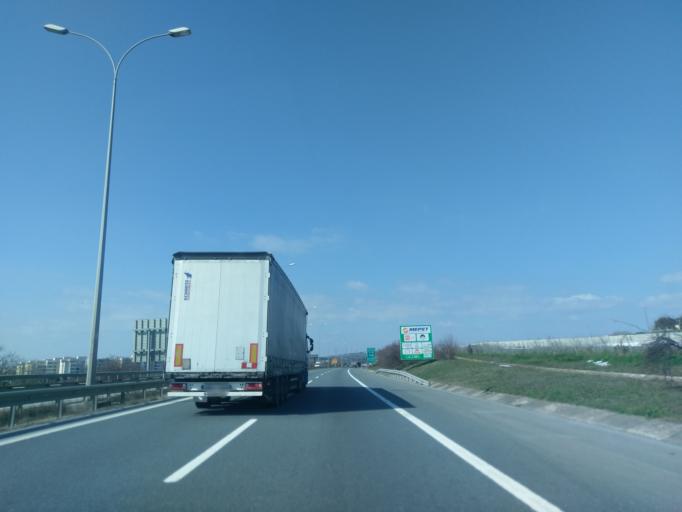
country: TR
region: Istanbul
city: Selimpasa
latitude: 41.0749
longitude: 28.3771
